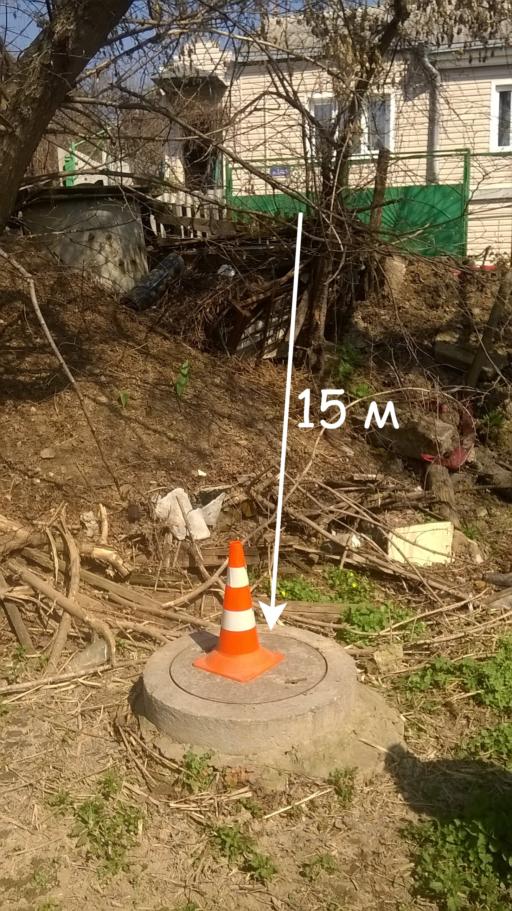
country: RU
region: Voronezj
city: Voronezh
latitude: 51.7079
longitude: 39.2347
